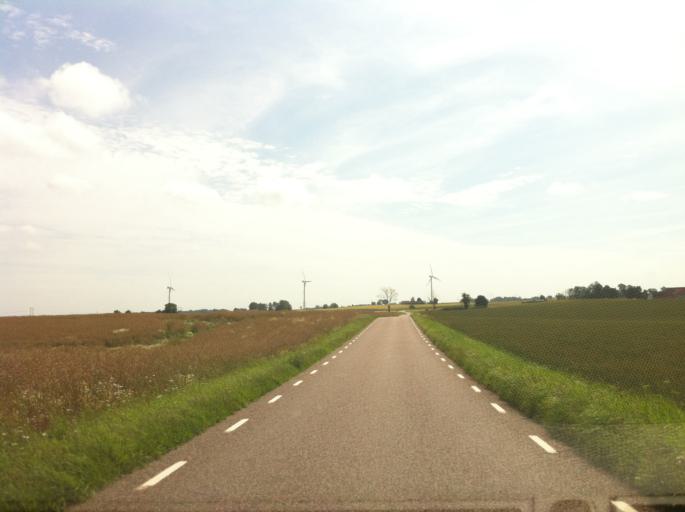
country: SE
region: Skane
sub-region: Skurups Kommun
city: Skurup
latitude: 55.4353
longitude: 13.4489
